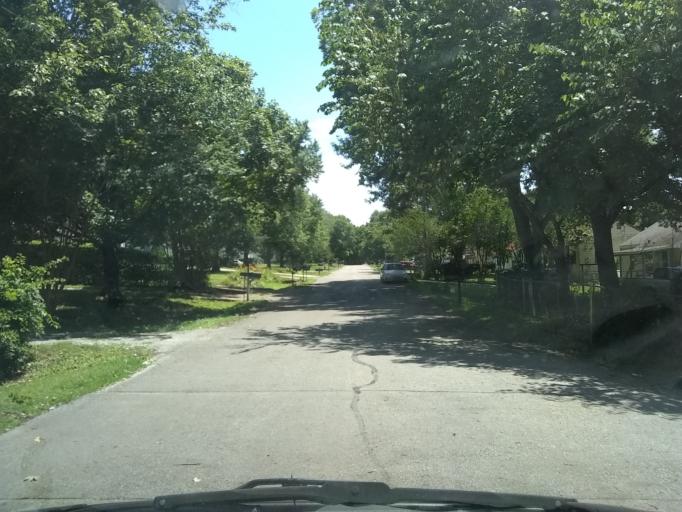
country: US
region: Tennessee
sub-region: Davidson County
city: Oak Hill
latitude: 36.1280
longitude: -86.6971
